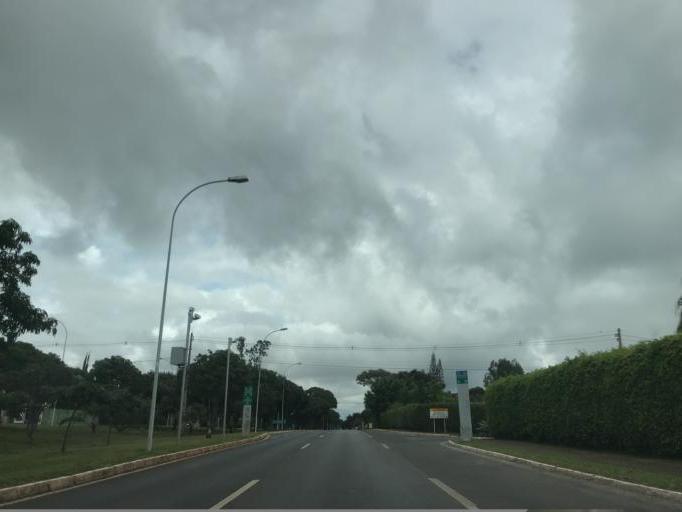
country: BR
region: Federal District
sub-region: Brasilia
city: Brasilia
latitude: -15.8416
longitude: -47.8423
